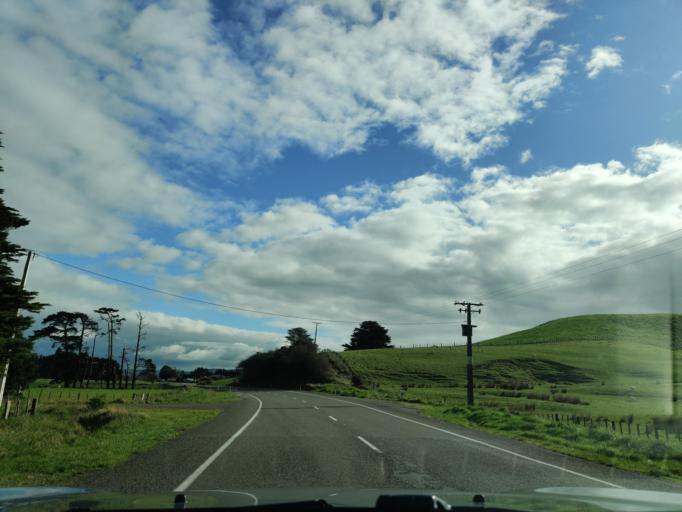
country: NZ
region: Manawatu-Wanganui
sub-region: Palmerston North City
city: Palmerston North
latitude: -40.3389
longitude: 175.8903
